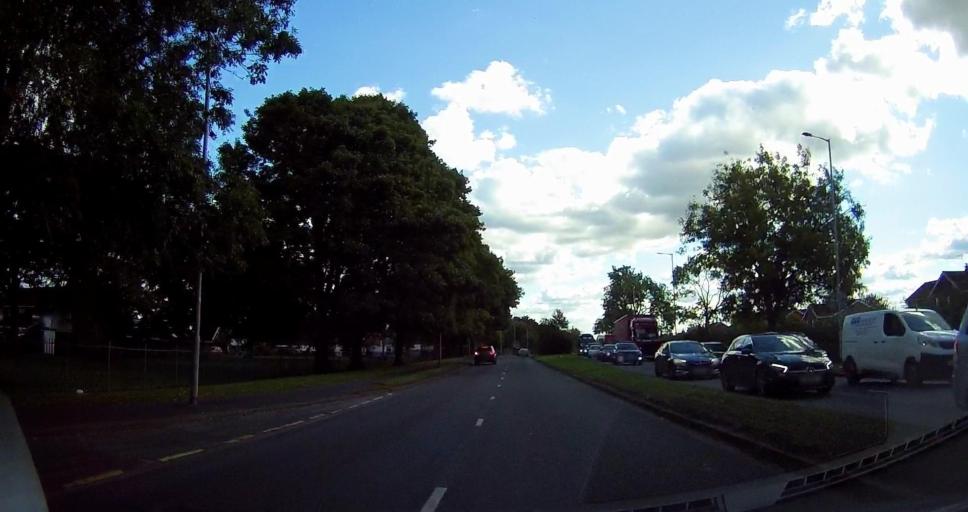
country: GB
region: England
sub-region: Staffordshire
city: Stafford
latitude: 52.8312
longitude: -2.1311
